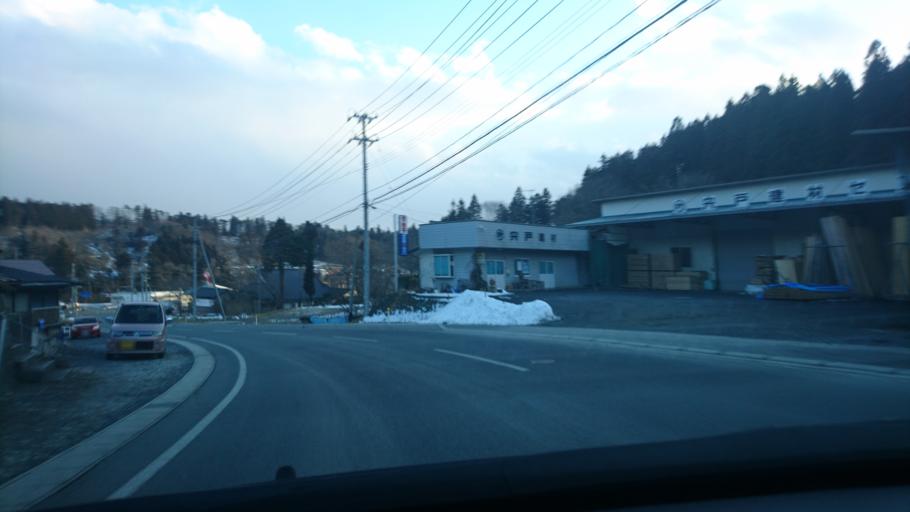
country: JP
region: Iwate
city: Ichinoseki
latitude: 38.9998
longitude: 141.3333
